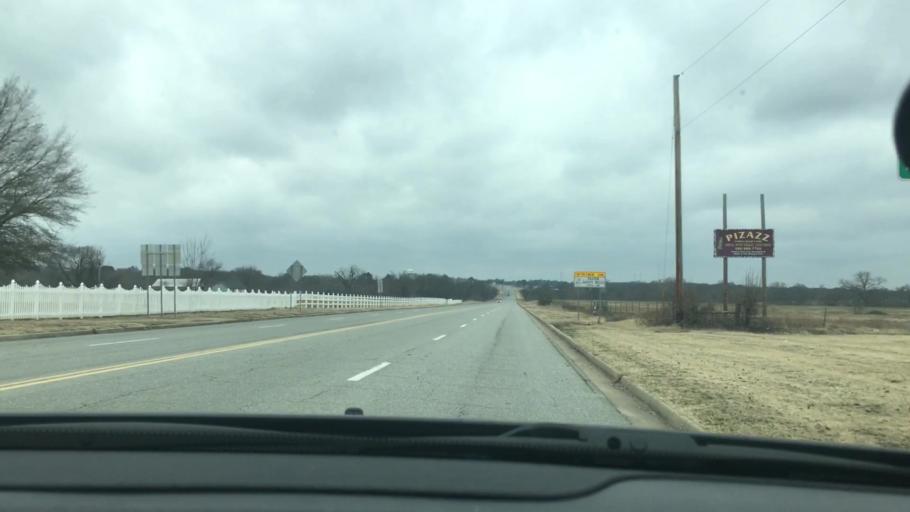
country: US
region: Oklahoma
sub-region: Atoka County
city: Atoka
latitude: 34.3925
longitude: -96.1456
